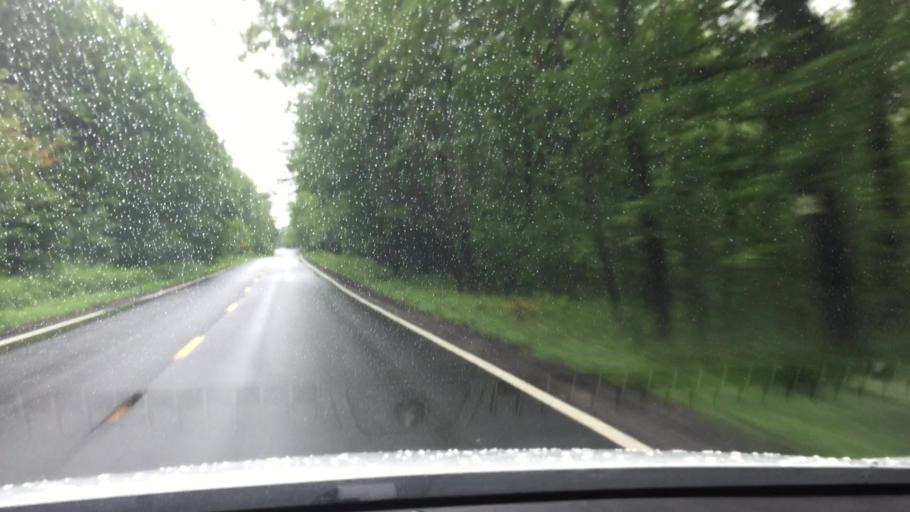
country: US
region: Massachusetts
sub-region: Berkshire County
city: Hinsdale
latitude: 42.3884
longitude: -73.1605
